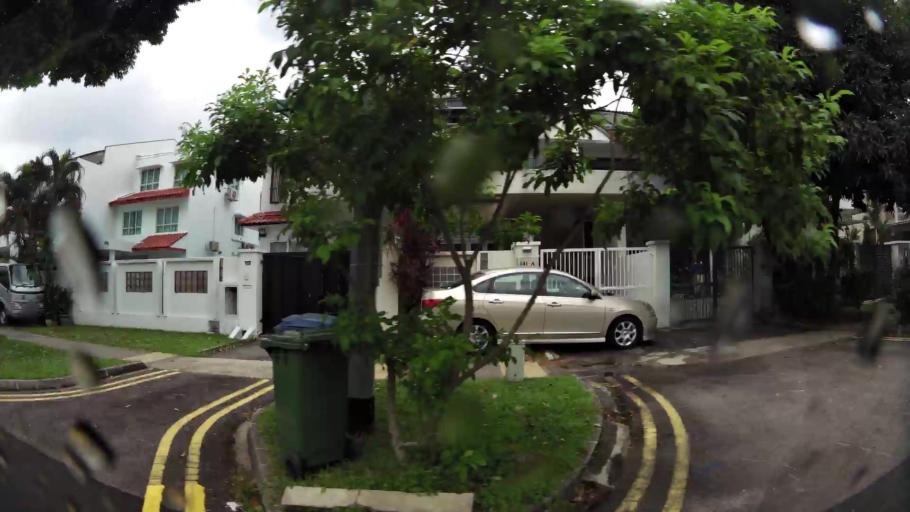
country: SG
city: Singapore
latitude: 1.3600
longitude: 103.8737
